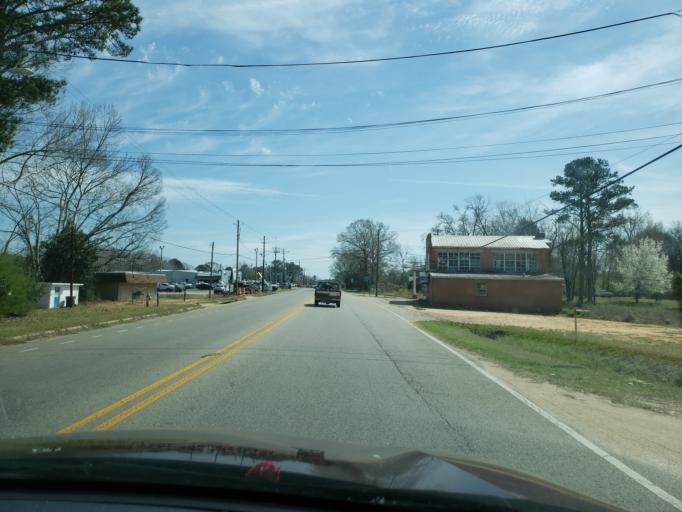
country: US
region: Alabama
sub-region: Elmore County
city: Tallassee
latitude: 32.5591
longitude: -85.9280
